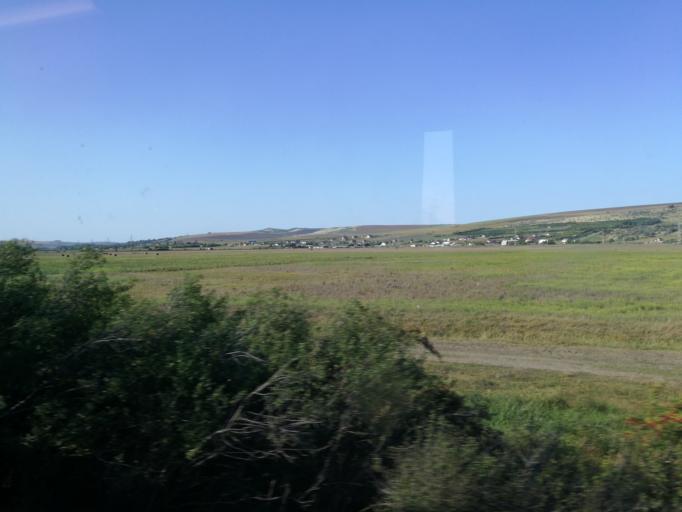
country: RO
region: Vaslui
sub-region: Municipiul Vaslui
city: Brodoc
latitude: 46.6648
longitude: 27.6794
